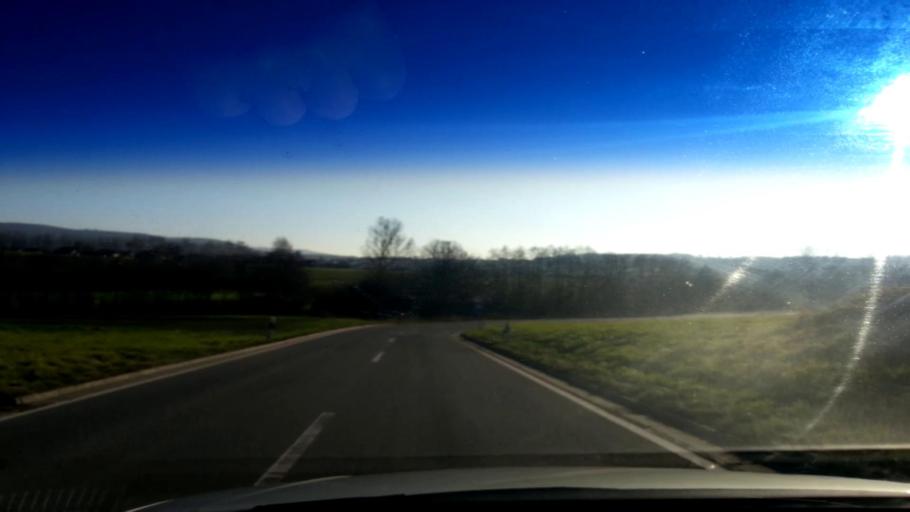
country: DE
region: Bavaria
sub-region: Upper Franconia
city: Litzendorf
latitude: 49.9177
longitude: 10.9976
